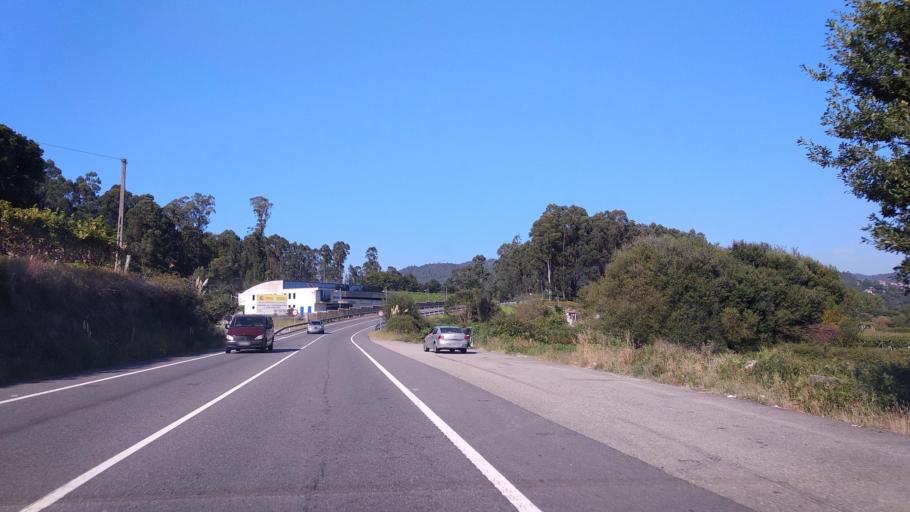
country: ES
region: Galicia
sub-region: Provincia de Pontevedra
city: Marin
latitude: 42.3526
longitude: -8.6413
